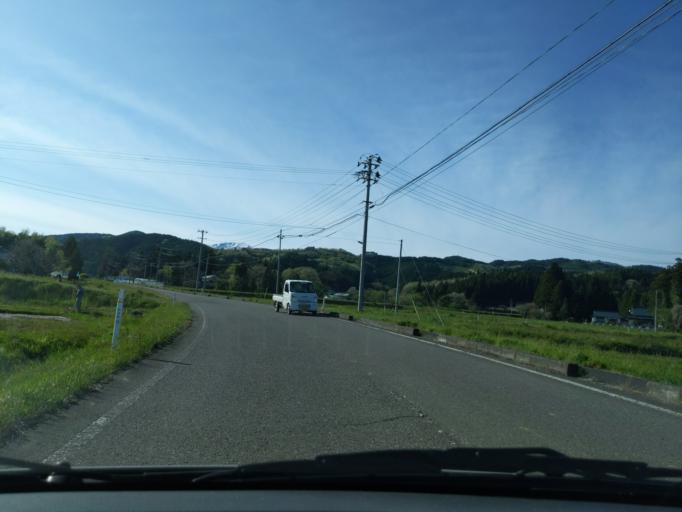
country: JP
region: Iwate
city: Ichinoseki
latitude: 38.8739
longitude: 140.8967
